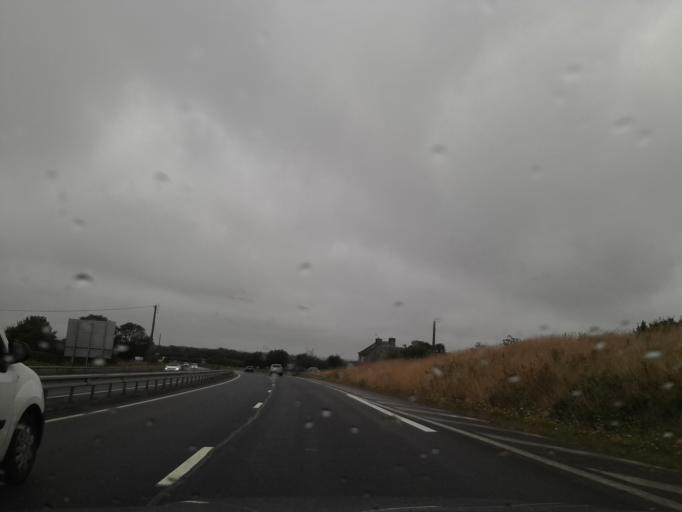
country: FR
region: Lower Normandy
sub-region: Departement de la Manche
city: Sainte-Mere-Eglise
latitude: 49.4129
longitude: -1.3218
